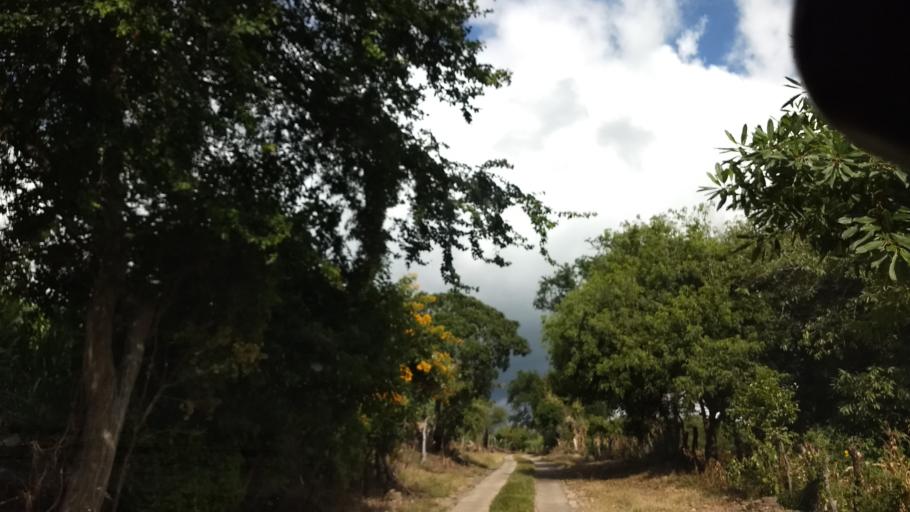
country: MX
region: Colima
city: Suchitlan
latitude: 19.4553
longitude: -103.7727
